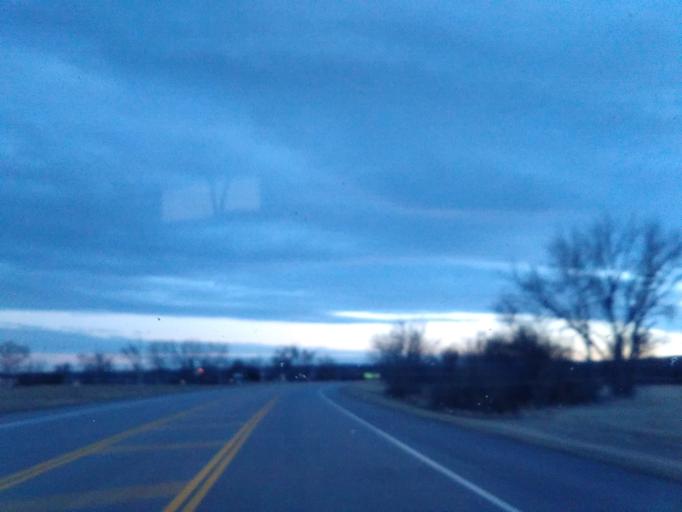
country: US
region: Nebraska
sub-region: Garden County
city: Oshkosh
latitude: 41.3248
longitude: -102.1281
